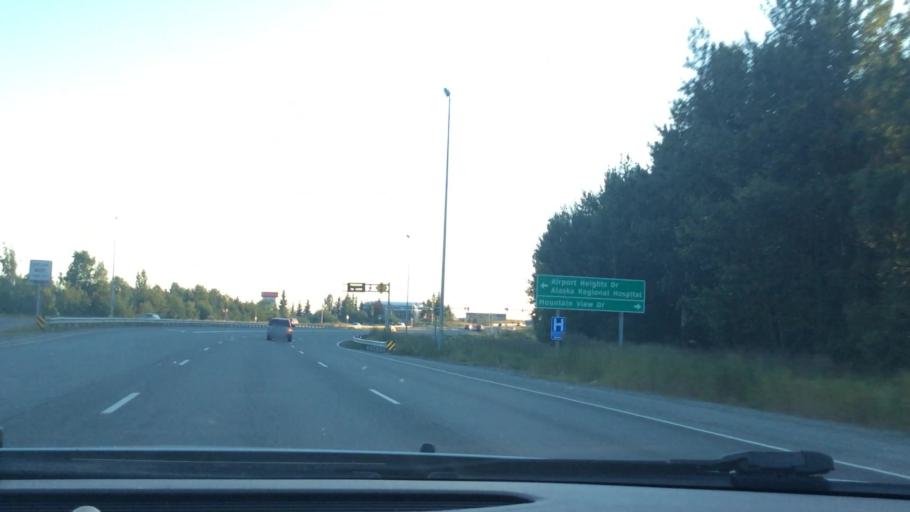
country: US
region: Alaska
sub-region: Anchorage Municipality
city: Anchorage
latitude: 61.2182
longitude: -149.8211
